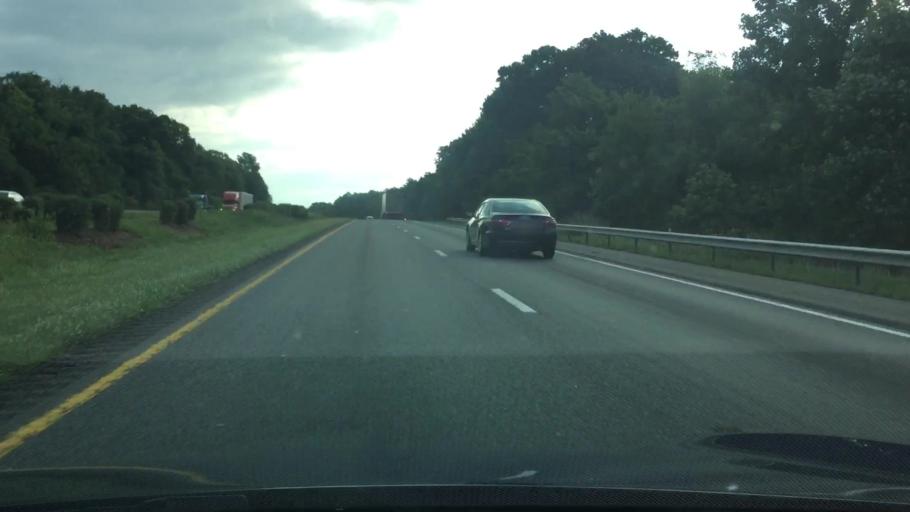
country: US
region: Virginia
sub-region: City of Salem
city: Salem
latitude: 37.2673
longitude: -80.1508
